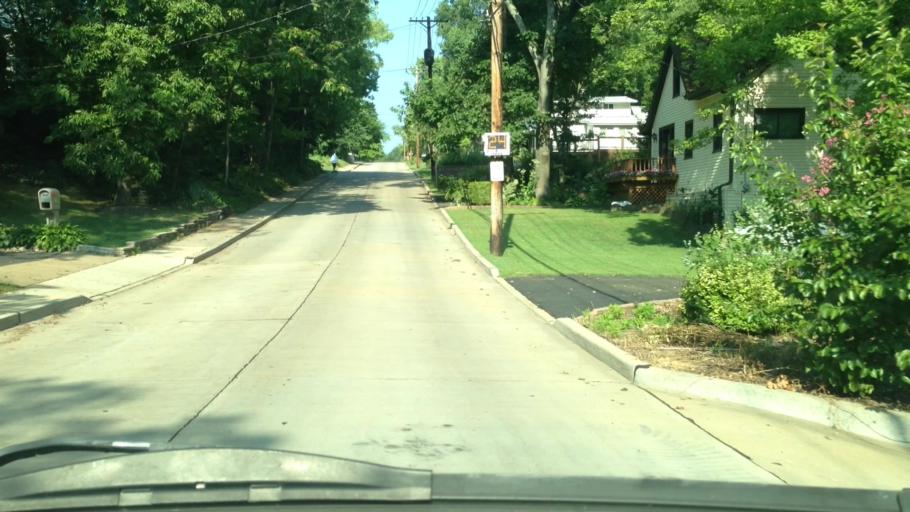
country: US
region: Missouri
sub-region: Saint Louis County
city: Des Peres
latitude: 38.5755
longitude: -90.4314
